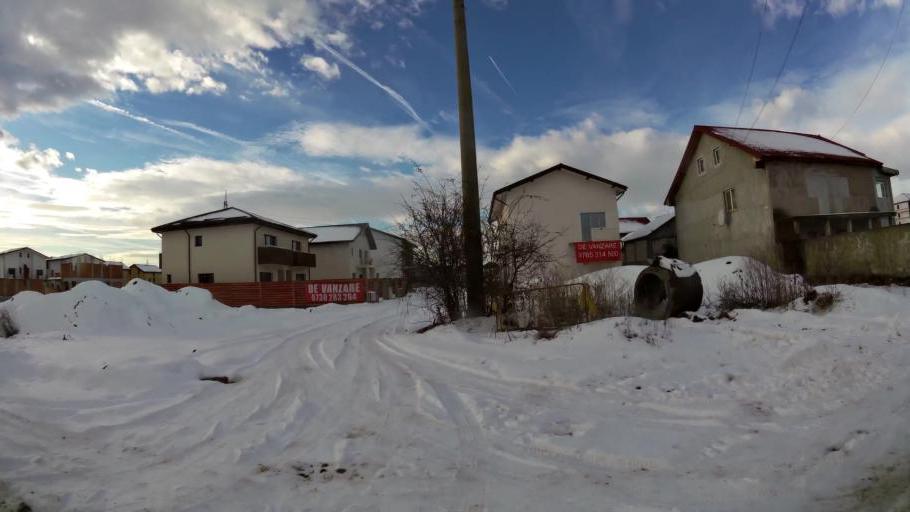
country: RO
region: Ilfov
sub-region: Comuna Fundeni-Dobroesti
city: Fundeni
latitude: 44.4653
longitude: 26.1773
